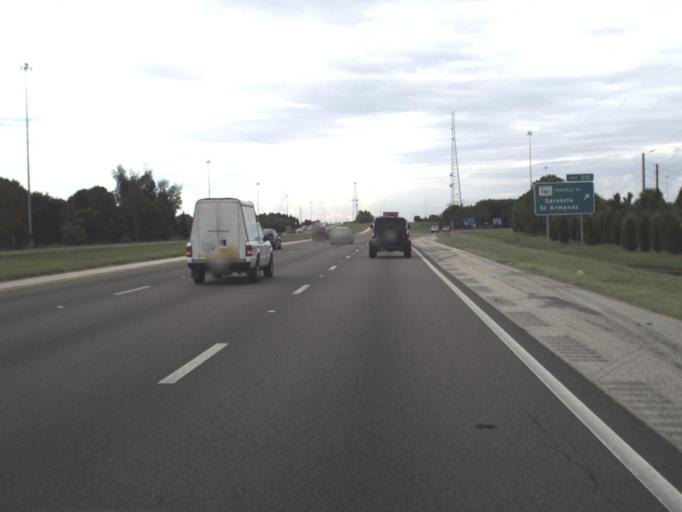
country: US
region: Florida
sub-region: Sarasota County
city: Fruitville
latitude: 27.3456
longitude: -82.4469
